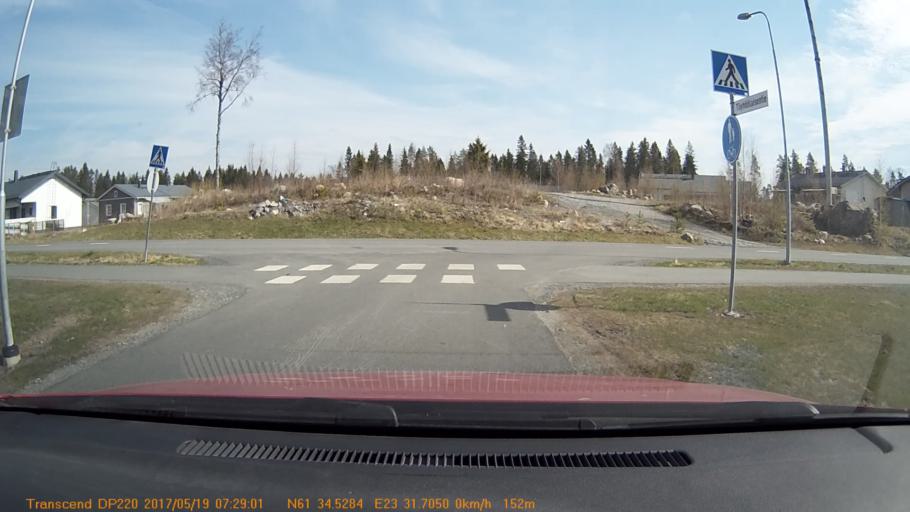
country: FI
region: Pirkanmaa
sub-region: Tampere
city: Yloejaervi
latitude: 61.5754
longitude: 23.5285
